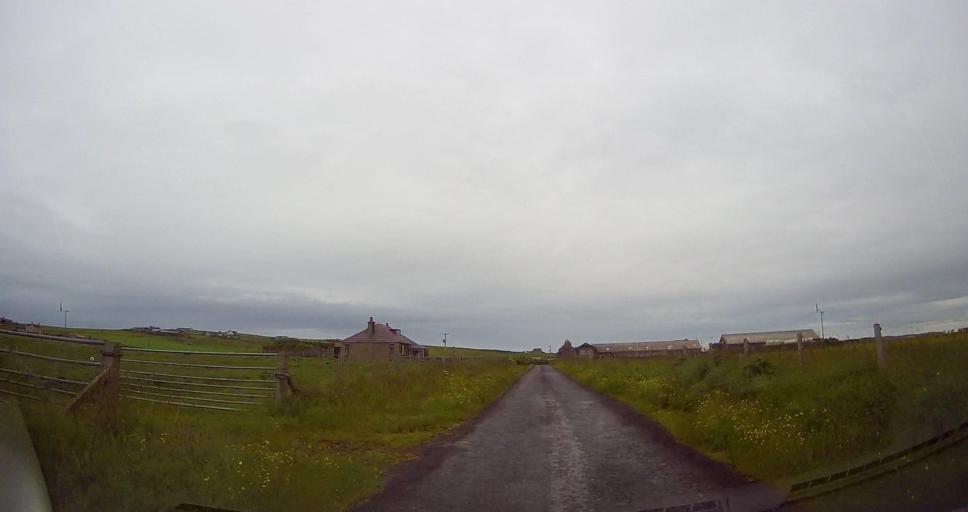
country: GB
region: Scotland
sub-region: Orkney Islands
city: Stromness
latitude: 59.1274
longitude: -3.2971
